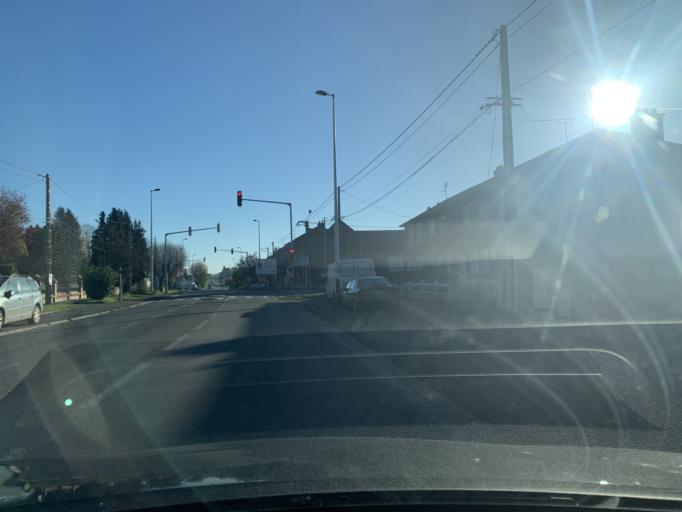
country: FR
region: Nord-Pas-de-Calais
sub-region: Departement du Nord
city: Cambrai
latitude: 50.1678
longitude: 3.2648
